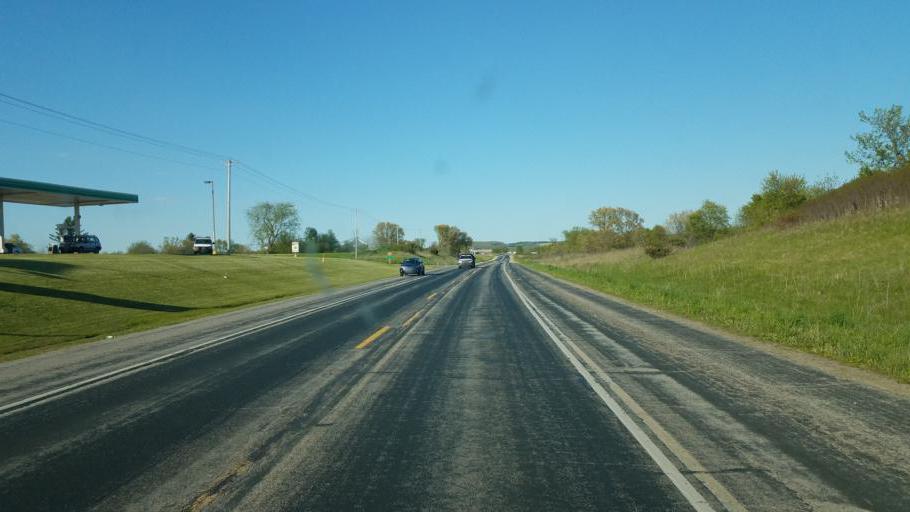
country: US
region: Wisconsin
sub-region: Vernon County
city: Hillsboro
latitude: 43.6606
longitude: -90.3274
